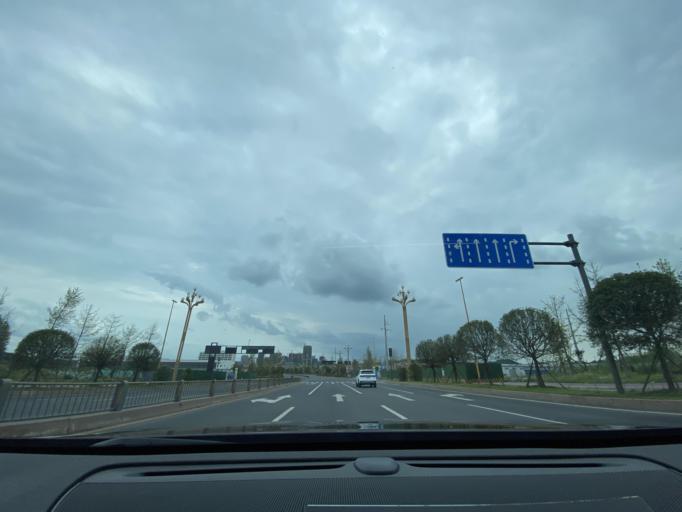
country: CN
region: Sichuan
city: Jiancheng
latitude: 30.4444
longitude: 104.4961
